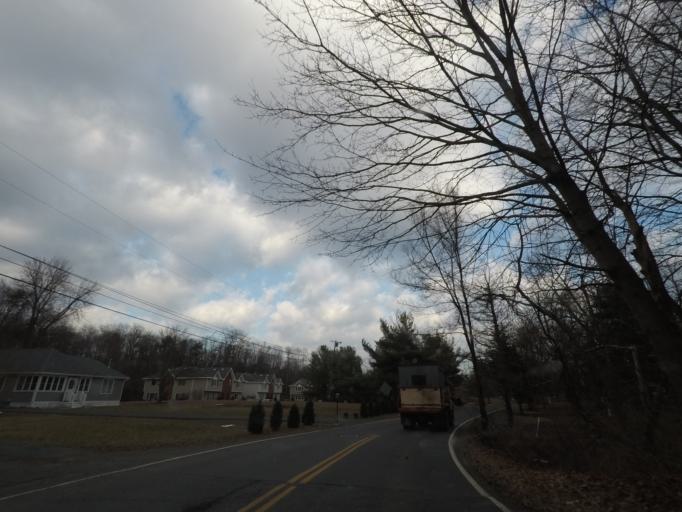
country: US
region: New York
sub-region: Albany County
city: McKownville
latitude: 42.6949
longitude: -73.8541
